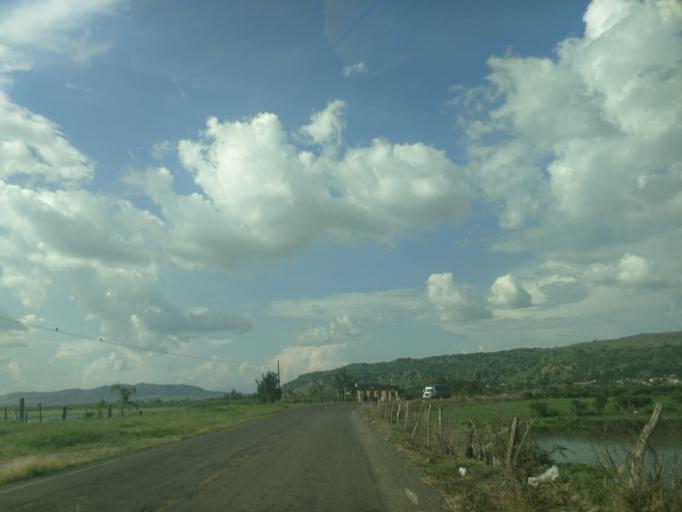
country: MX
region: Jalisco
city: Antonio Escobedo
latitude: 20.9030
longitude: -103.9950
